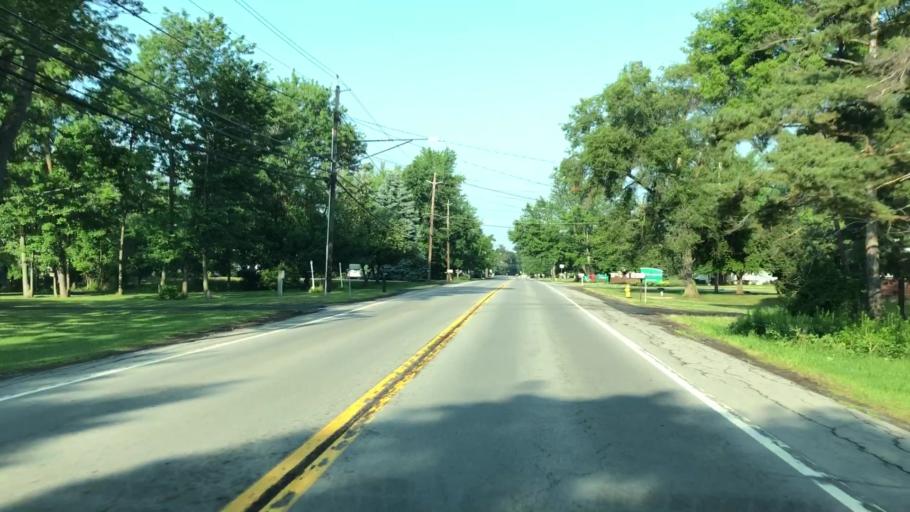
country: US
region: New York
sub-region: Erie County
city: Orchard Park
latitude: 42.8329
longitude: -78.7202
